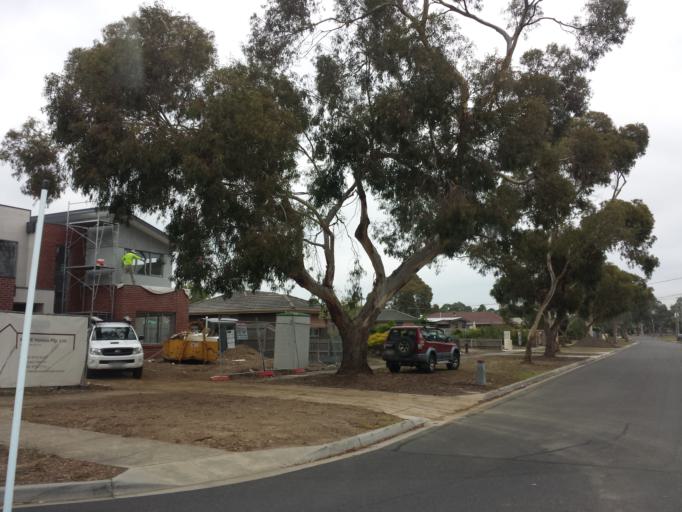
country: AU
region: Victoria
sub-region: Knox
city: Knoxfield
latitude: -37.8839
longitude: 145.2681
